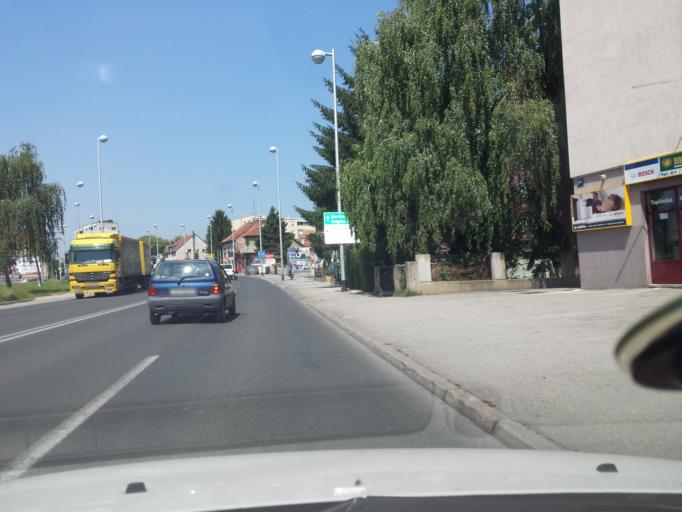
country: HR
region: Grad Zagreb
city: Jankomir
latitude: 45.8126
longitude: 15.9085
